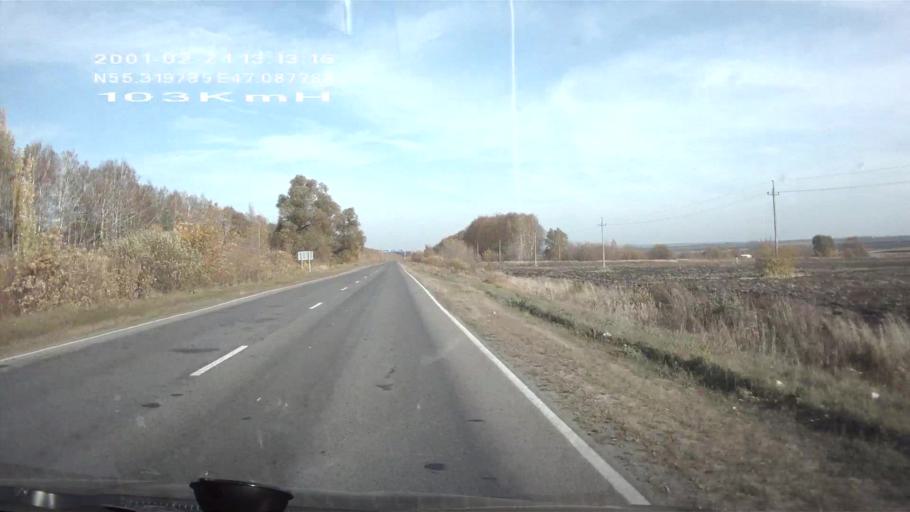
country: RU
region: Chuvashia
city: Ibresi
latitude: 55.3197
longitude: 47.0876
